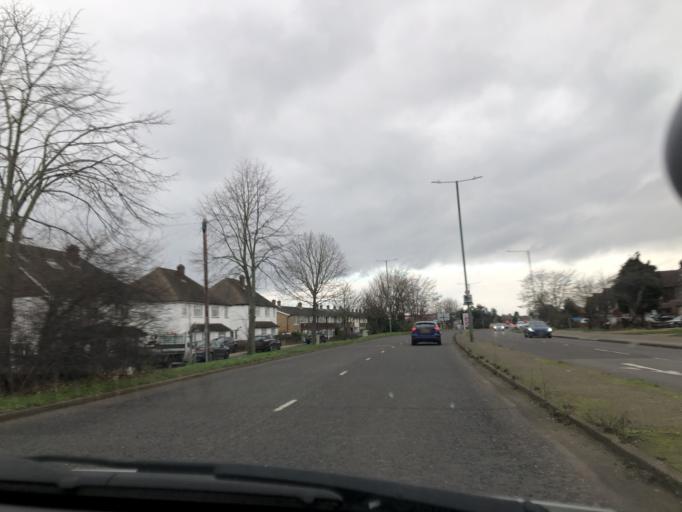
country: GB
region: England
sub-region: Kent
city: Dartford
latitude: 51.4394
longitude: 0.1992
